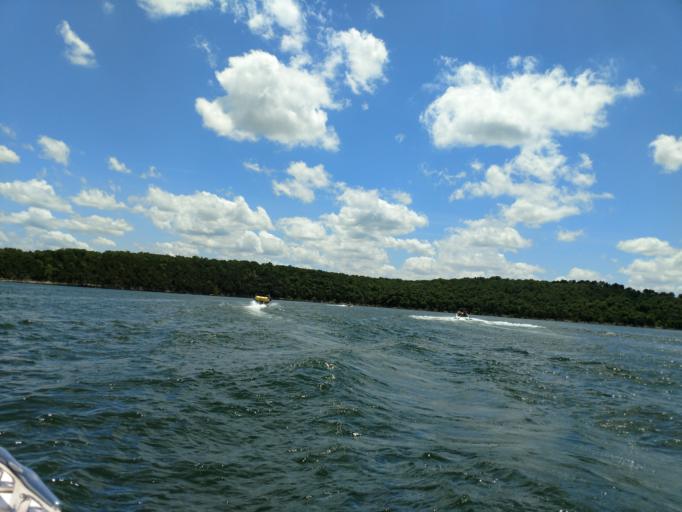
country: US
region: Missouri
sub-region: Barry County
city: Shell Knob
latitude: 36.5960
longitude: -93.5421
